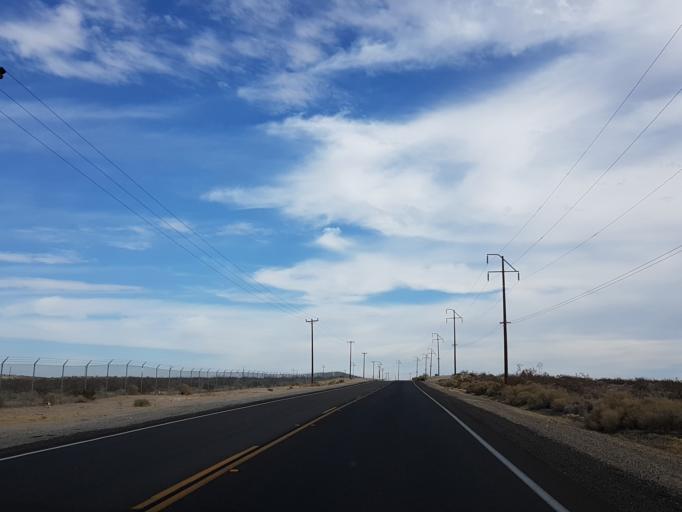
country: US
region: California
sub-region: Kern County
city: Ridgecrest
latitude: 35.6226
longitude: -117.6041
